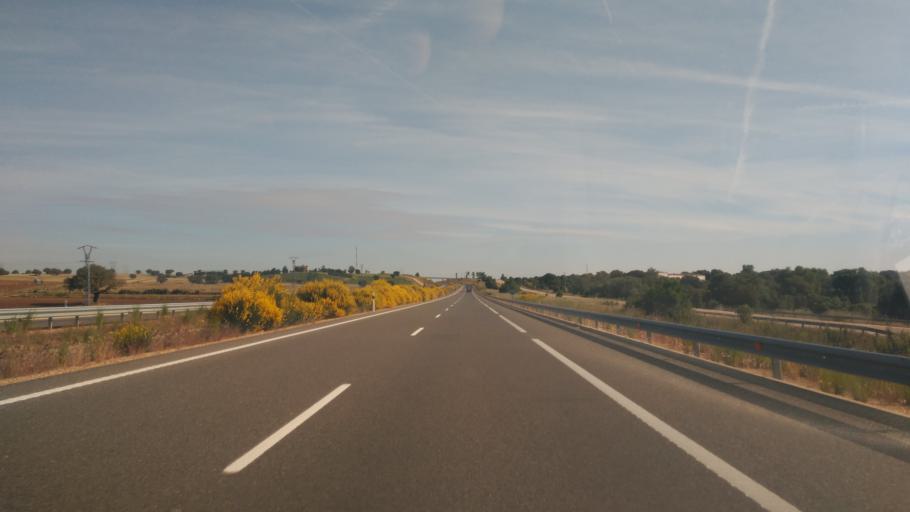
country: ES
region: Castille and Leon
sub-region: Provincia de Salamanca
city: Topas
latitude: 41.1685
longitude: -5.6953
